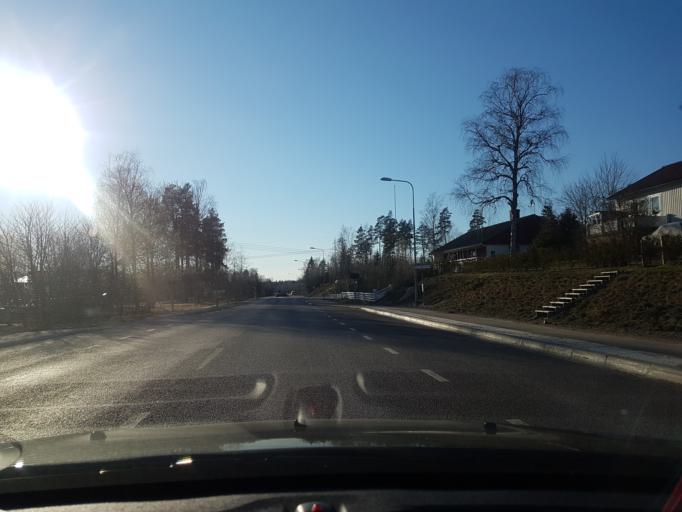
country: SE
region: Uppsala
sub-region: Enkopings Kommun
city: Orsundsbro
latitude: 59.8870
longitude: 17.1938
